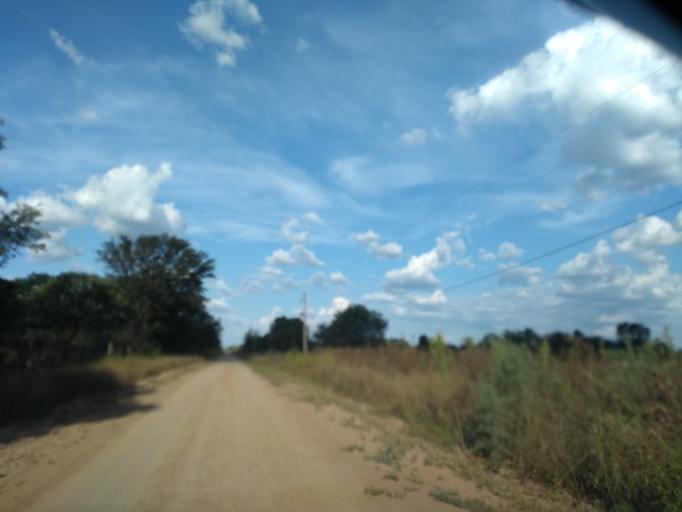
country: AR
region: Chaco
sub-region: Departamento de Quitilipi
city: Quitilipi
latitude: -26.7480
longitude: -60.2687
